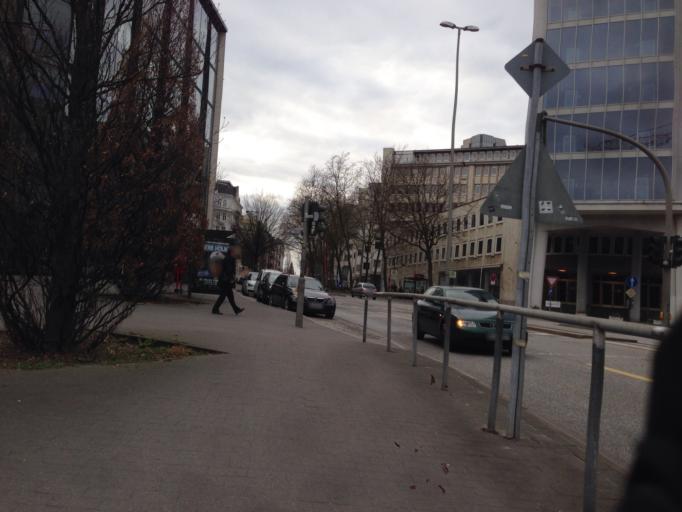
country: DE
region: Hamburg
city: Neustadt
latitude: 53.5521
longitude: 9.9853
